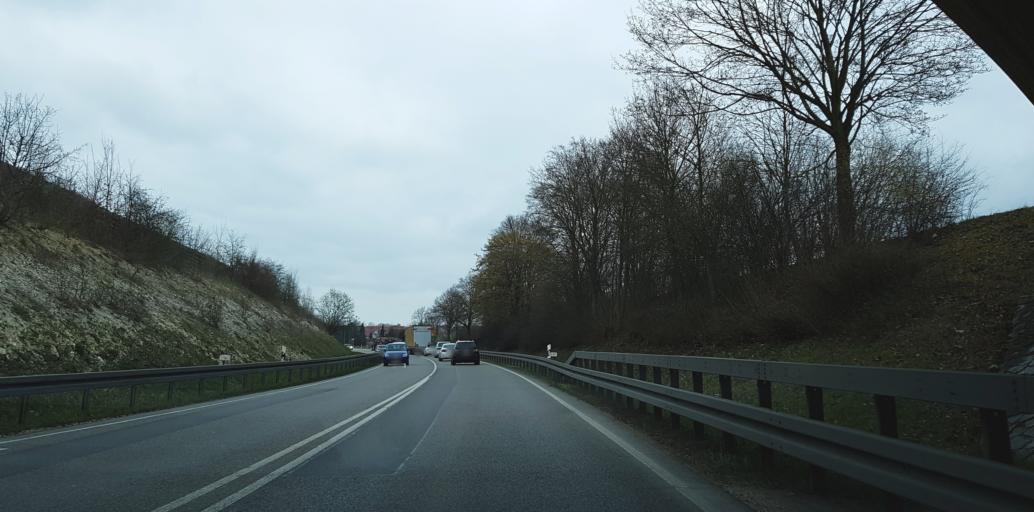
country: DE
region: Baden-Wuerttemberg
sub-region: Tuebingen Region
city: Ehingen
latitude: 48.2867
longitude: 9.7363
